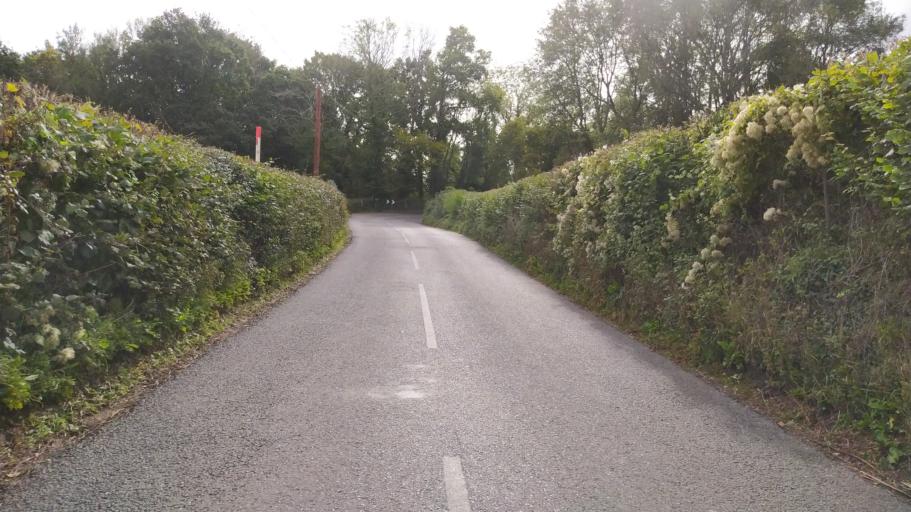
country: GB
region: England
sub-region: Hampshire
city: Romsey
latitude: 51.0264
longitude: -1.5342
